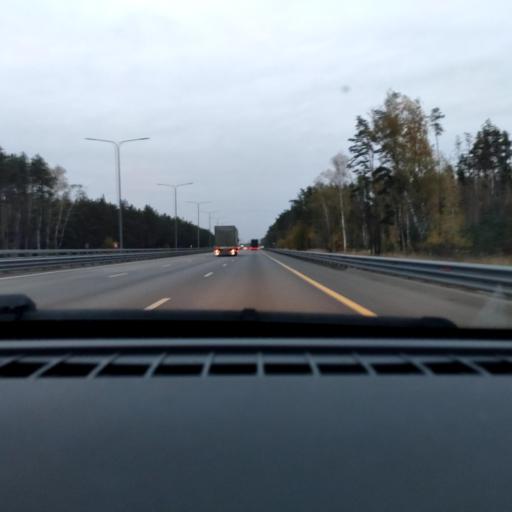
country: RU
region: Voronezj
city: Somovo
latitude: 51.7173
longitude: 39.3088
